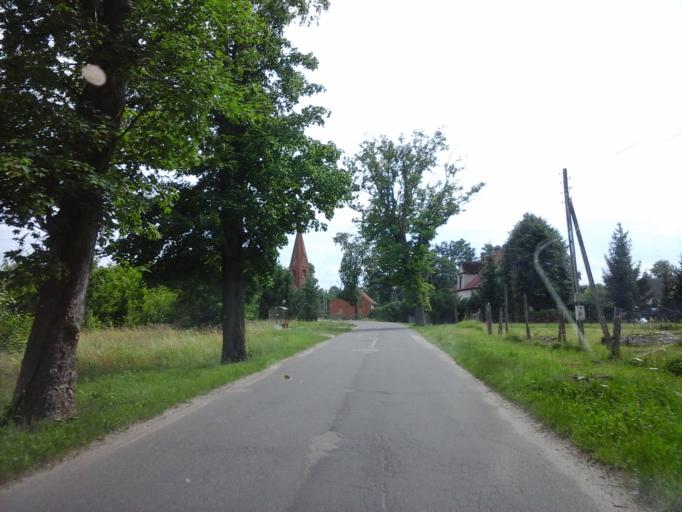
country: PL
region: Lubusz
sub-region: Powiat strzelecko-drezdenecki
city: Dobiegniew
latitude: 53.0800
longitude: 15.7800
